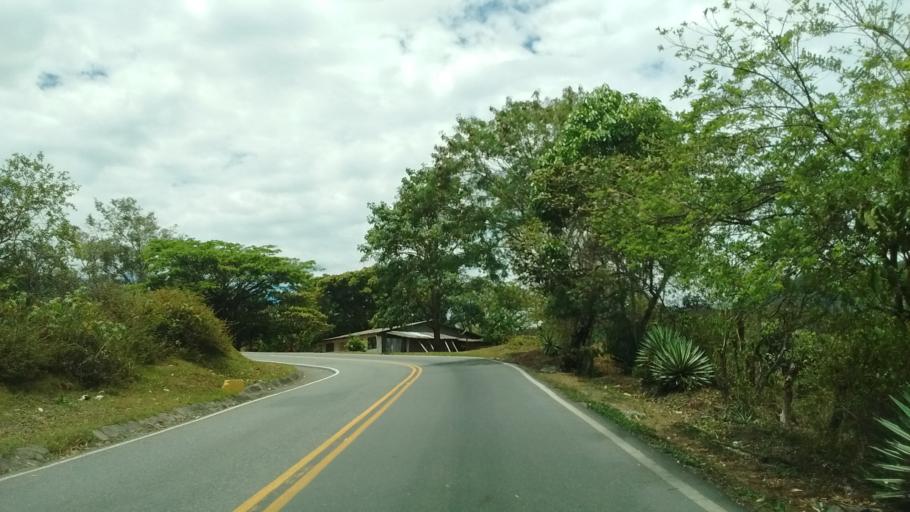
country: CO
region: Cauca
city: La Sierra
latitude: 2.2168
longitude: -76.7989
